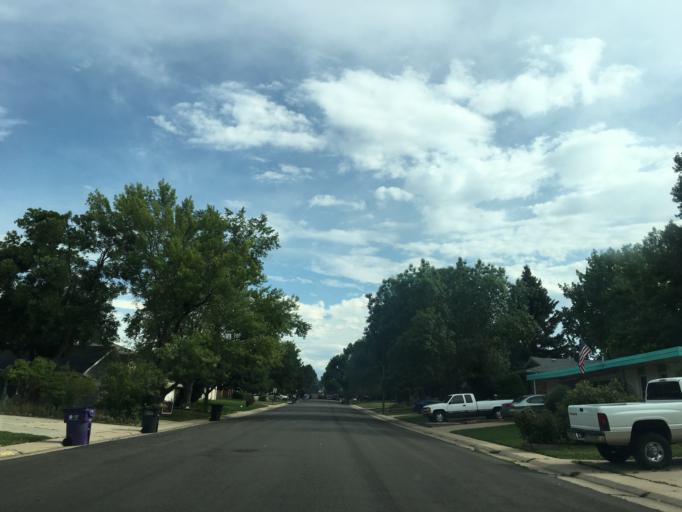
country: US
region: Colorado
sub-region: Jefferson County
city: Lakewood
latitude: 39.6773
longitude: -105.0621
